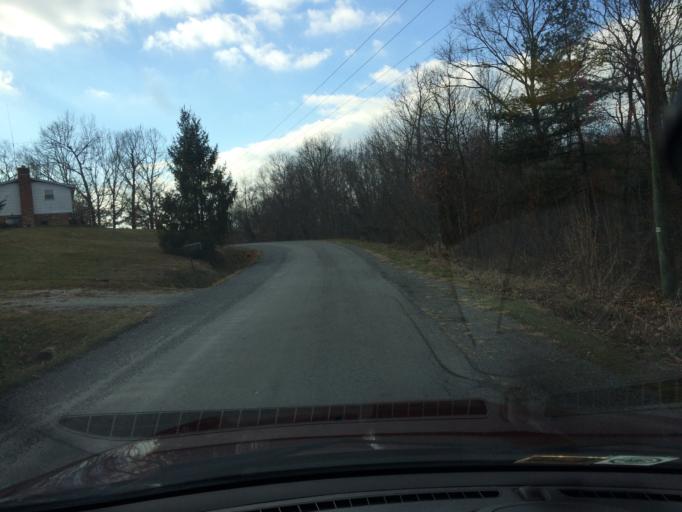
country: US
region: Virginia
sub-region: Alleghany County
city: Clifton Forge
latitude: 37.8205
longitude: -79.8045
